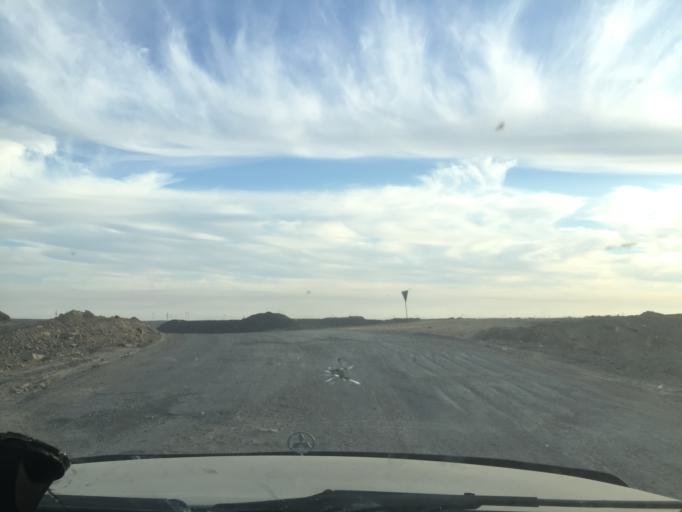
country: KZ
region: Almaty Oblysy
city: Ulken
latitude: 45.1549
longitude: 73.9460
